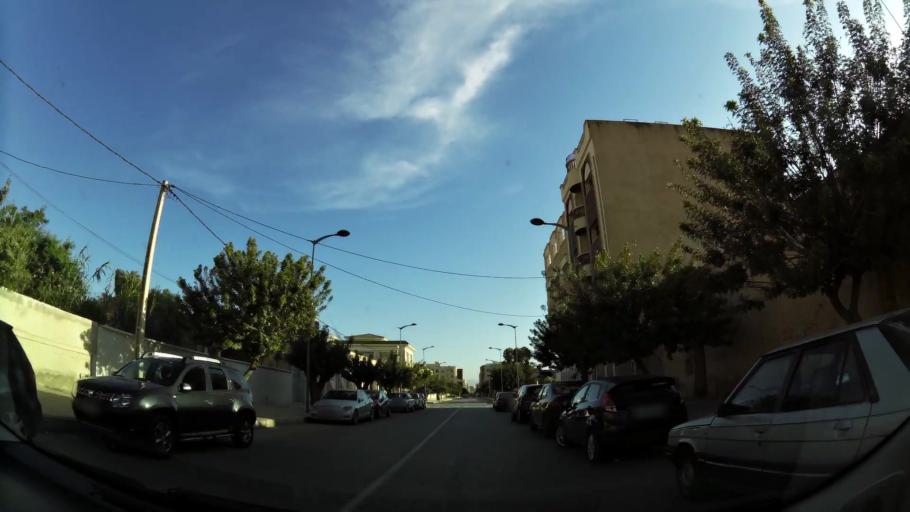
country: MA
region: Oriental
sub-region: Oujda-Angad
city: Oujda
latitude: 34.6929
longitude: -1.9125
